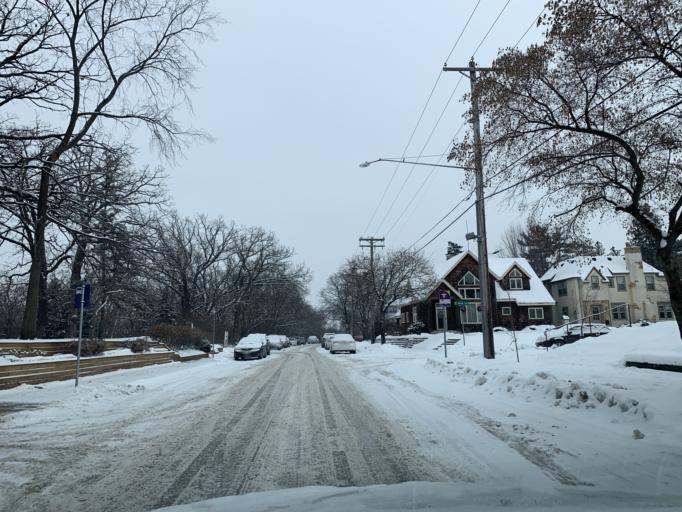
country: US
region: Minnesota
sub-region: Hennepin County
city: Saint Louis Park
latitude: 44.9537
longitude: -93.3266
